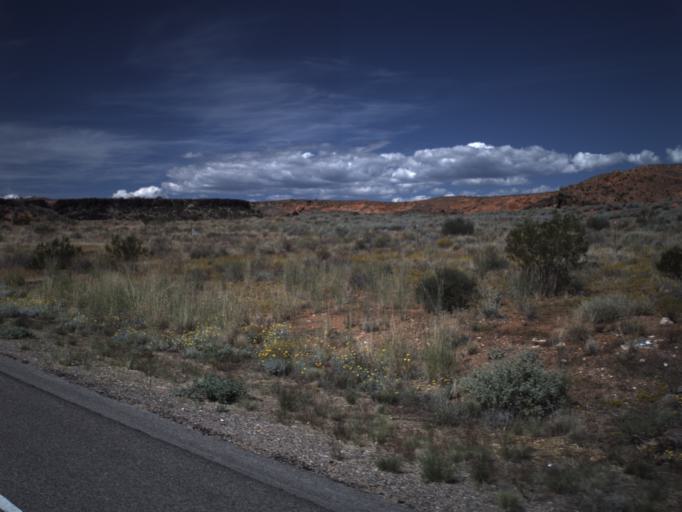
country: US
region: Utah
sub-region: Washington County
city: Santa Clara
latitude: 37.1602
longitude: -113.6061
